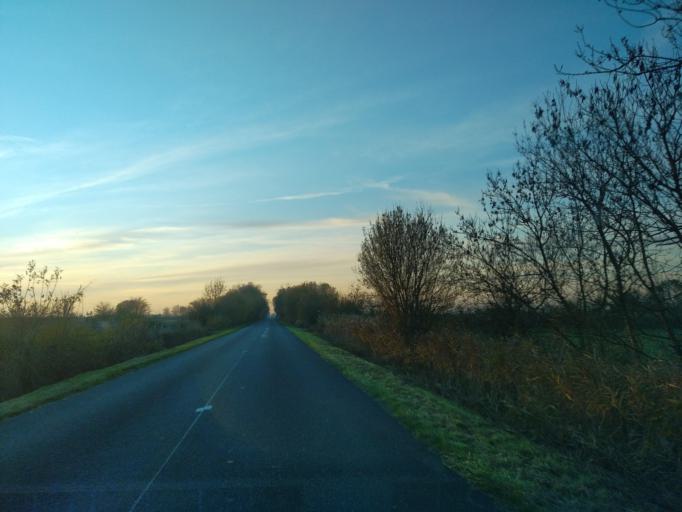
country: FR
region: Pays de la Loire
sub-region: Departement de la Vendee
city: Maillezais
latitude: 46.3783
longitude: -0.7605
